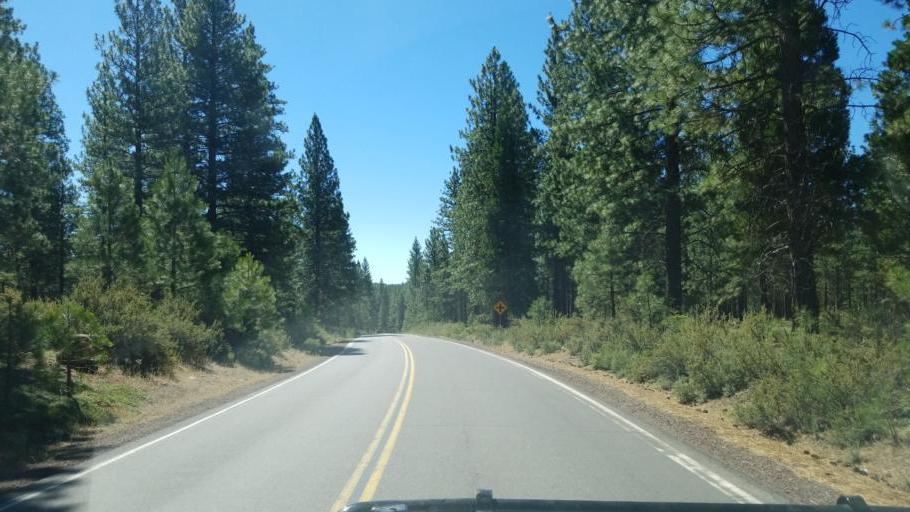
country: US
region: California
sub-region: Lassen County
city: Susanville
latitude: 40.4302
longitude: -120.7299
